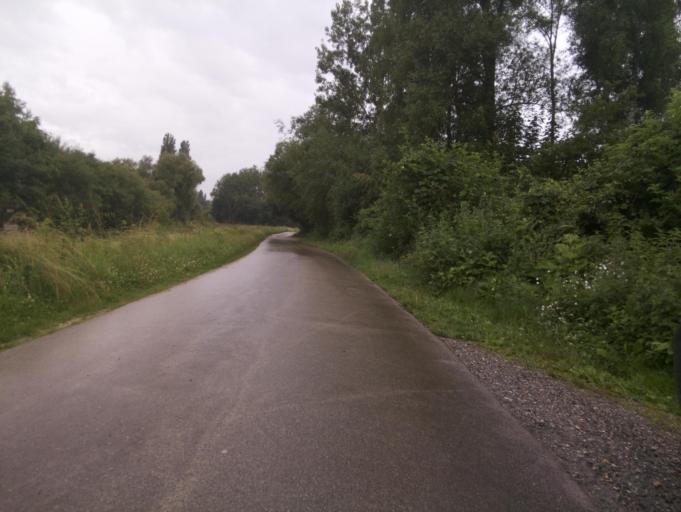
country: FR
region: Picardie
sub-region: Departement de la Somme
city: Ailly-sur-Somme
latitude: 49.9350
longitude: 2.1847
